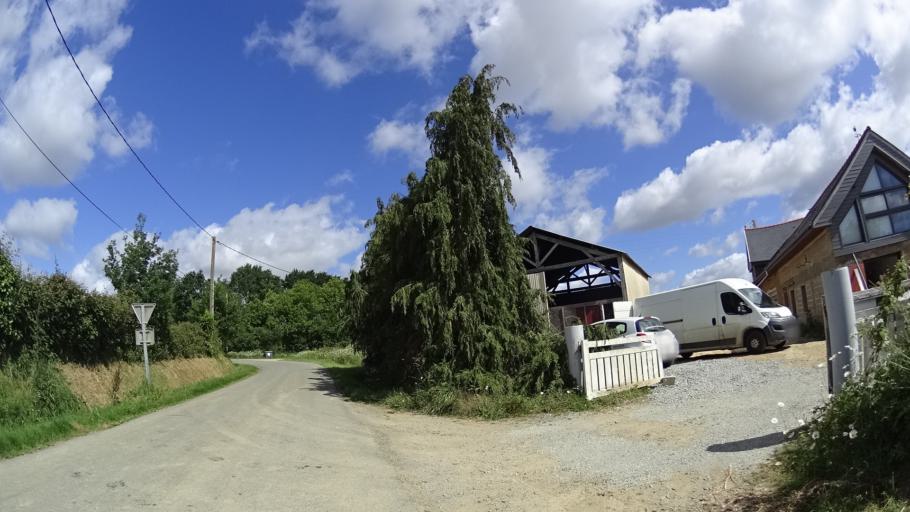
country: FR
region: Brittany
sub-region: Departement d'Ille-et-Vilaine
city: Montreuil-le-Gast
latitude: 48.2328
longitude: -1.7404
